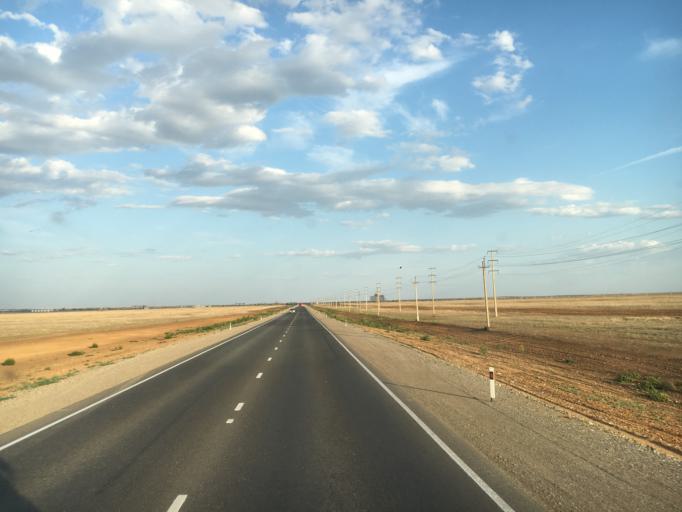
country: KZ
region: Aqtoebe
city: Aqtobe
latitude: 50.2208
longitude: 57.1937
